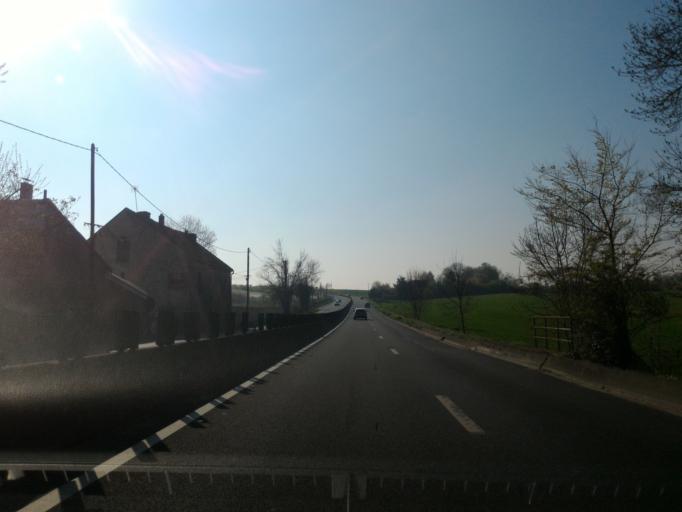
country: FR
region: Ile-de-France
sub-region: Departement du Val-de-Marne
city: Ormesson-sur-Marne
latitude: 48.7878
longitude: 2.5624
